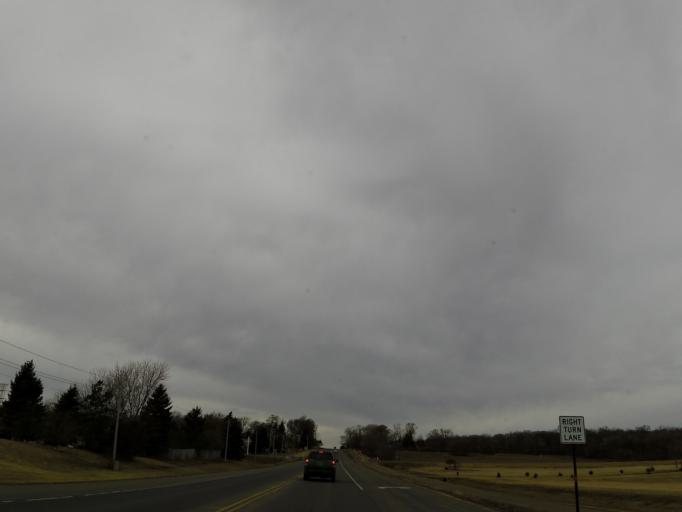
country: US
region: Minnesota
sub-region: Washington County
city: Cottage Grove
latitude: 44.8481
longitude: -92.9196
